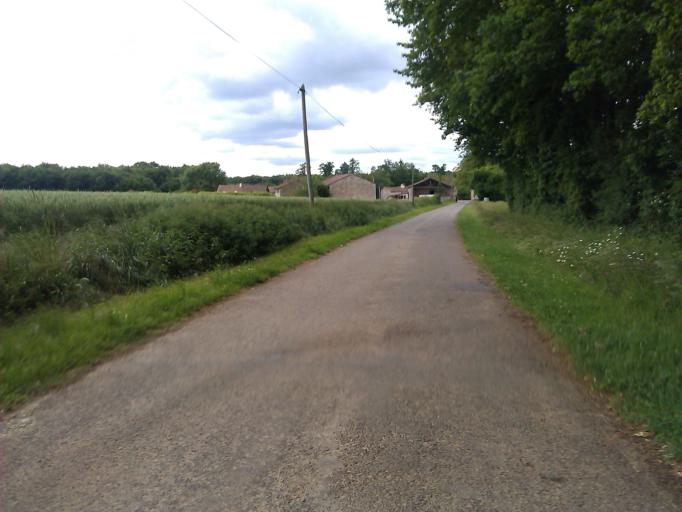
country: FR
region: Poitou-Charentes
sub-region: Departement de la Charente
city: Nanteuil-en-Vallee
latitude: 45.9623
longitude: 0.2846
